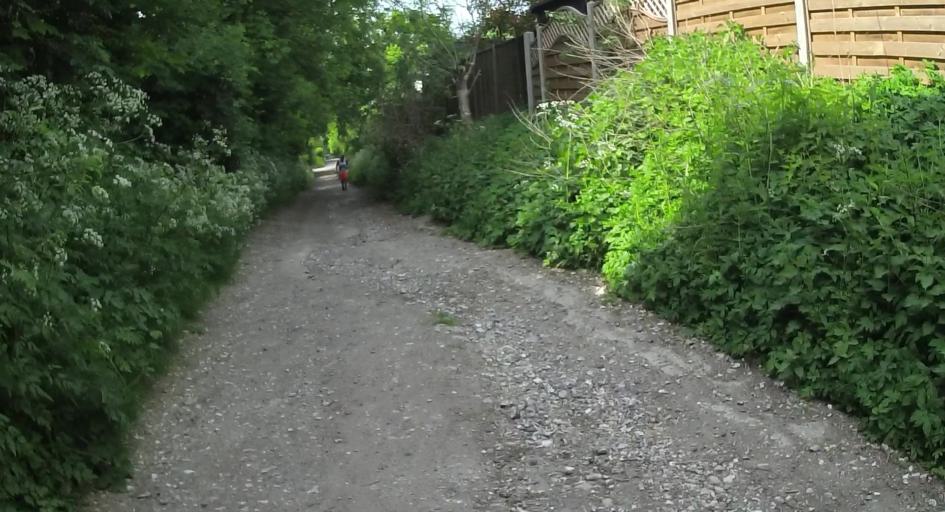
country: GB
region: England
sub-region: Hampshire
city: Kingsclere
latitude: 51.3232
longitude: -1.2407
